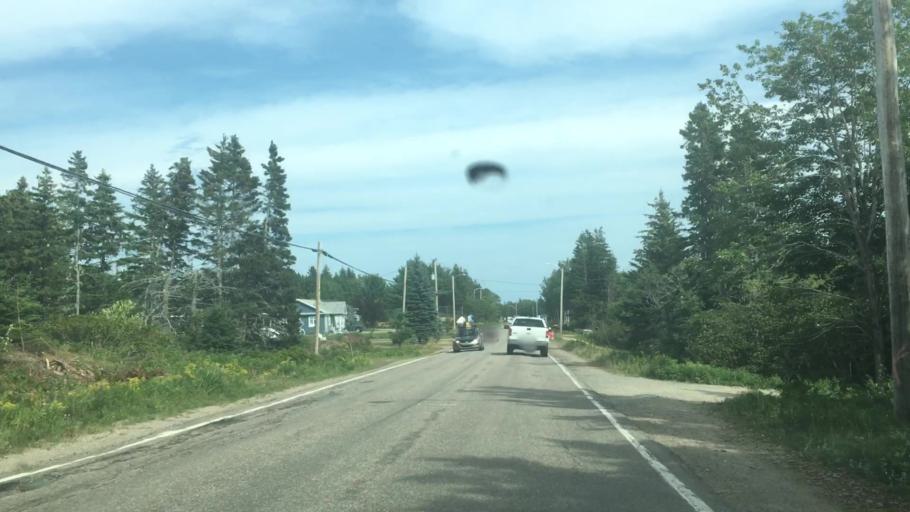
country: CA
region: Nova Scotia
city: Sydney Mines
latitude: 46.6898
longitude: -60.3875
